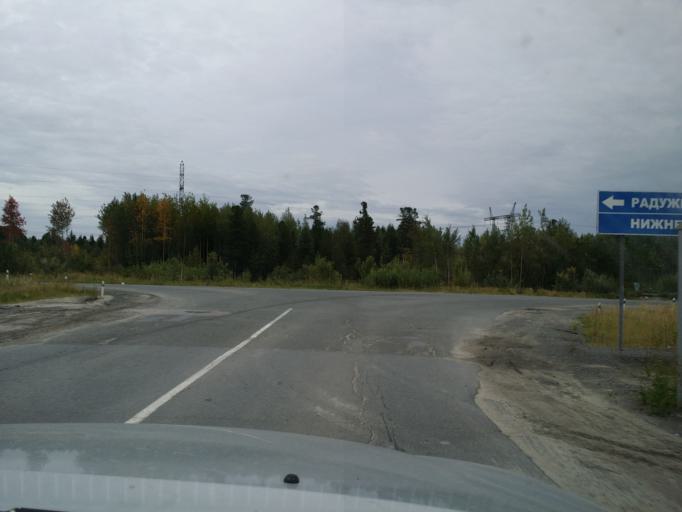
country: RU
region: Khanty-Mansiyskiy Avtonomnyy Okrug
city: Izluchinsk
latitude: 61.1657
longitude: 76.9255
